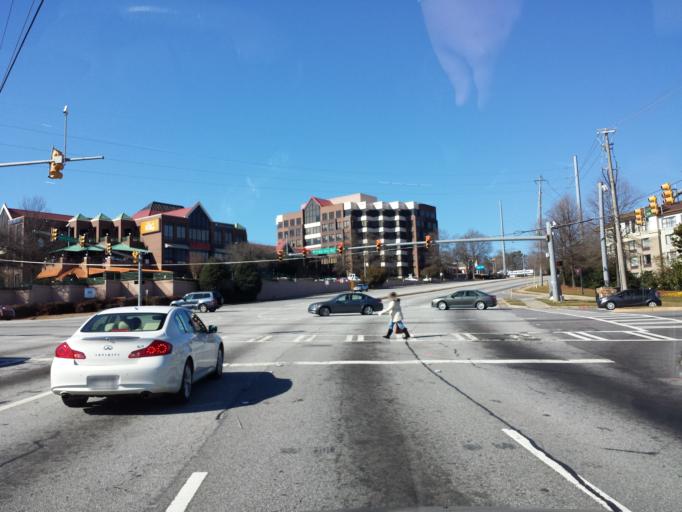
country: US
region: Georgia
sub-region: Cobb County
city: Vinings
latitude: 33.9054
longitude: -84.4638
